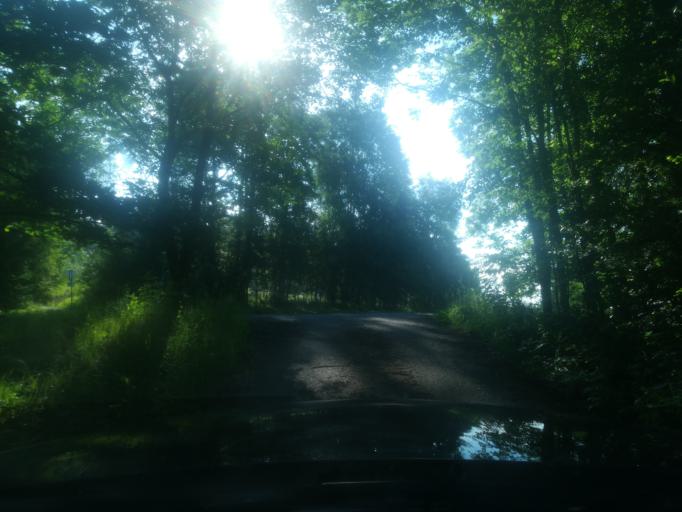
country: AT
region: Upper Austria
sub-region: Politischer Bezirk Perg
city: Perg
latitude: 48.3309
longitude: 14.5922
